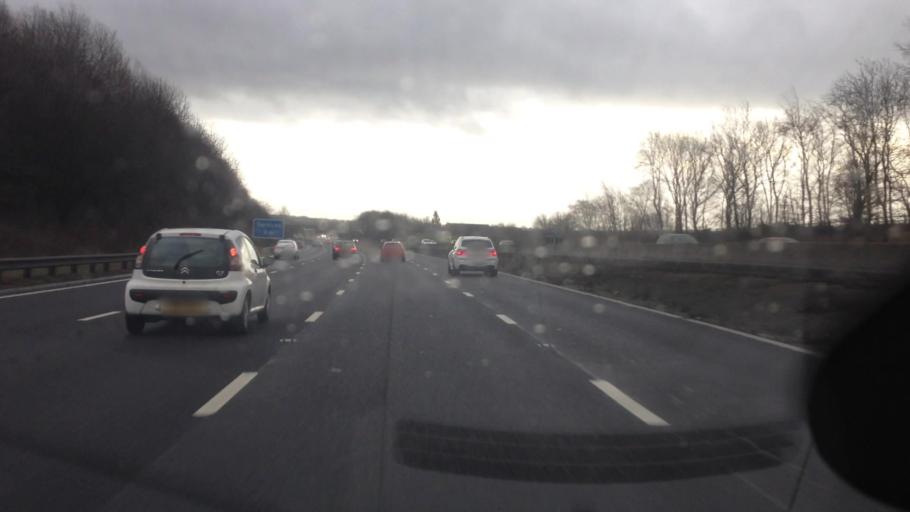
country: GB
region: England
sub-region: City and Borough of Wakefield
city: Horbury
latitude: 53.6708
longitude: -1.5474
